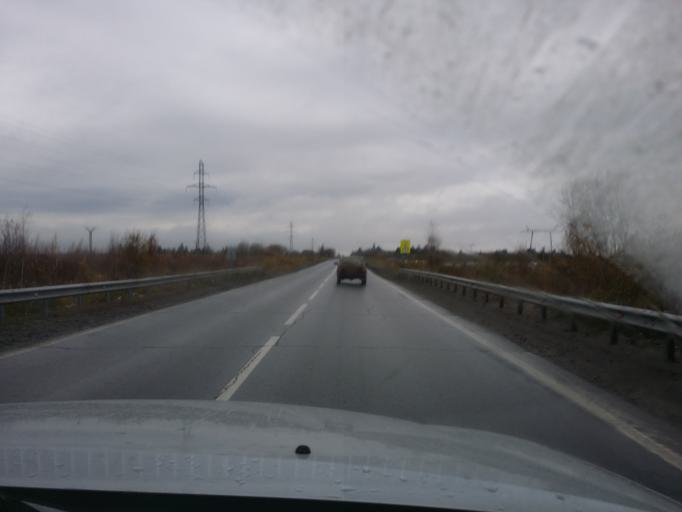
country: RU
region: Khanty-Mansiyskiy Avtonomnyy Okrug
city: Megion
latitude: 61.1037
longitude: 75.9433
